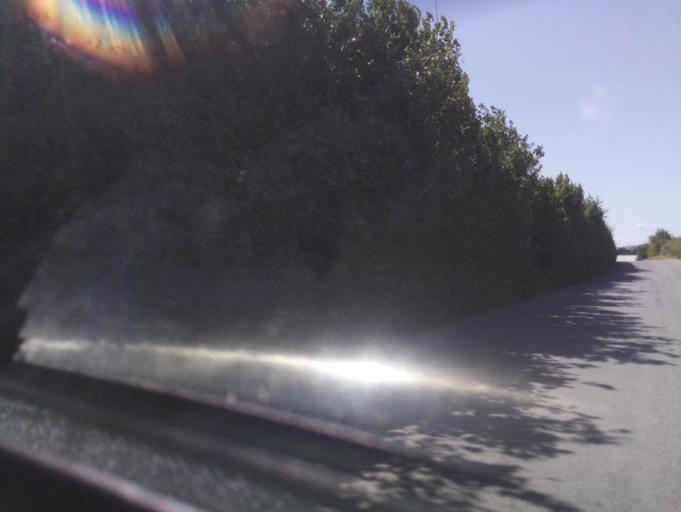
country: GB
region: England
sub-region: Devon
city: Ipplepen
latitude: 50.4865
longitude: -3.6222
